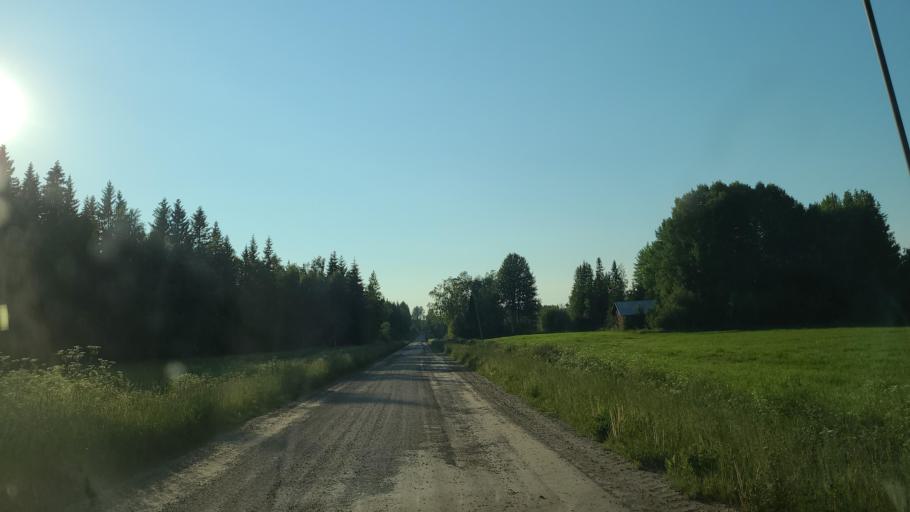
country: SE
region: Vaesterbotten
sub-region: Skelleftea Kommun
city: Burea
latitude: 64.4056
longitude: 21.3632
